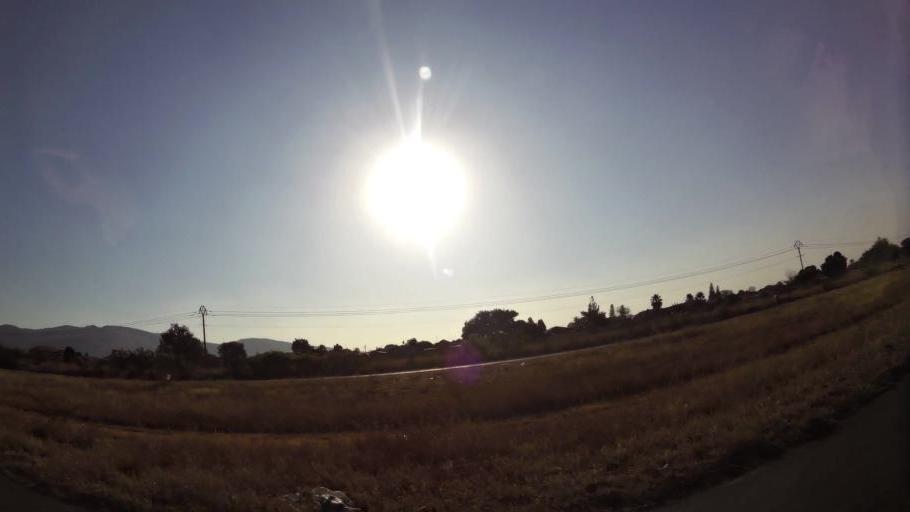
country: ZA
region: North-West
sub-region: Bojanala Platinum District Municipality
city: Rustenburg
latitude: -25.6503
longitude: 27.2236
